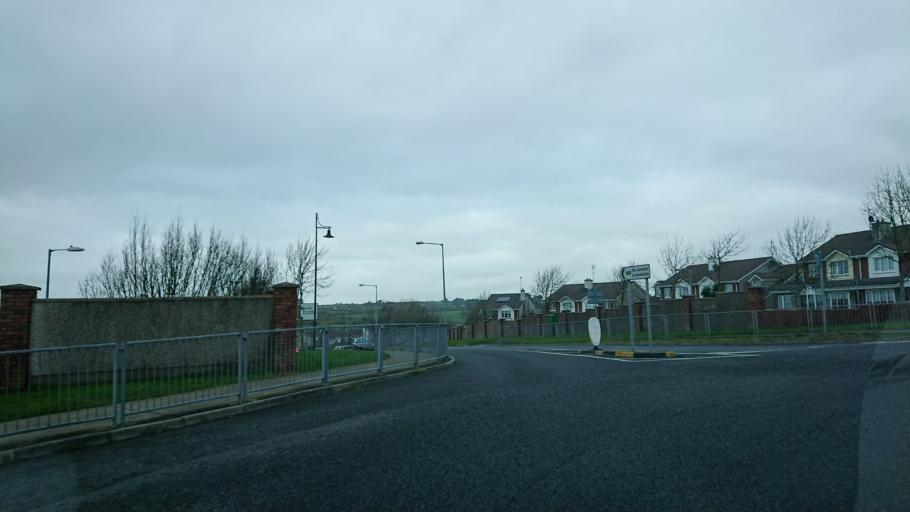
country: IE
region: Munster
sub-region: Waterford
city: Tra Mhor
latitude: 52.1652
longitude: -7.1624
